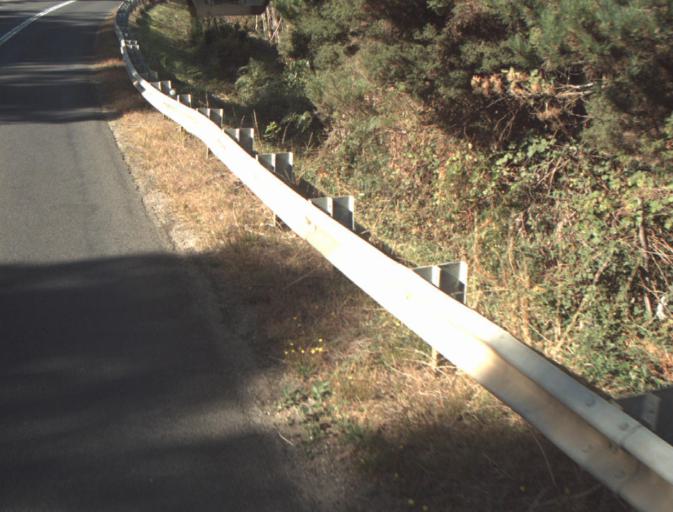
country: AU
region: Tasmania
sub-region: Launceston
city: Mayfield
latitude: -41.3364
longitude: 147.1704
